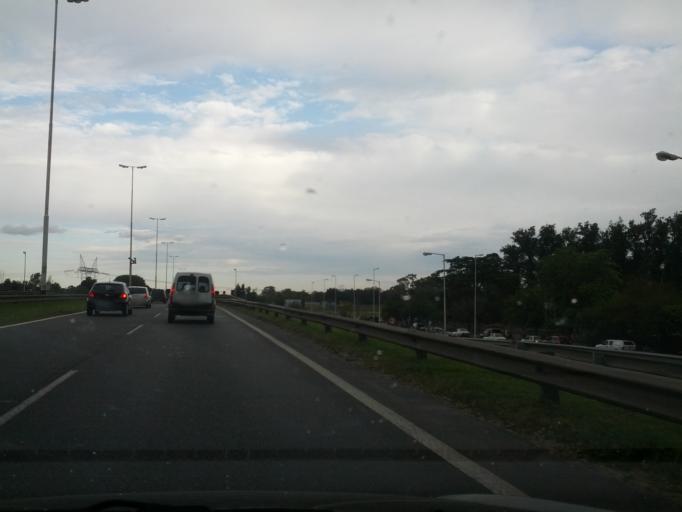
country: AR
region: Buenos Aires
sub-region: Partido de General Rodriguez
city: General Rodriguez
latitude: -34.5781
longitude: -59.0173
